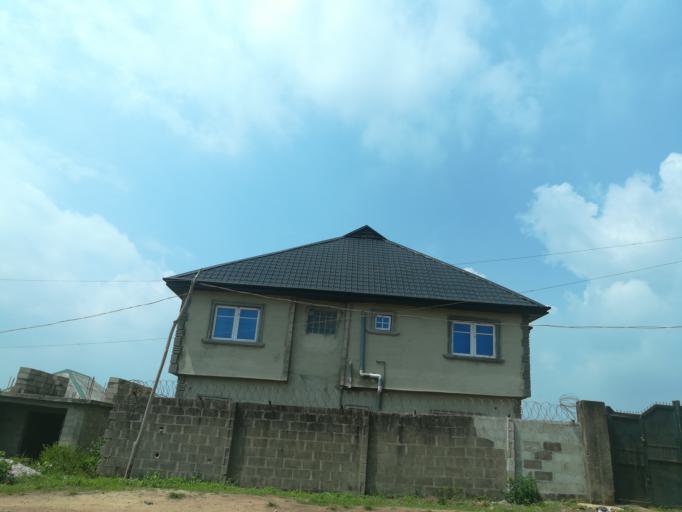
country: NG
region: Lagos
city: Ikorodu
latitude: 6.5930
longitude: 3.6405
